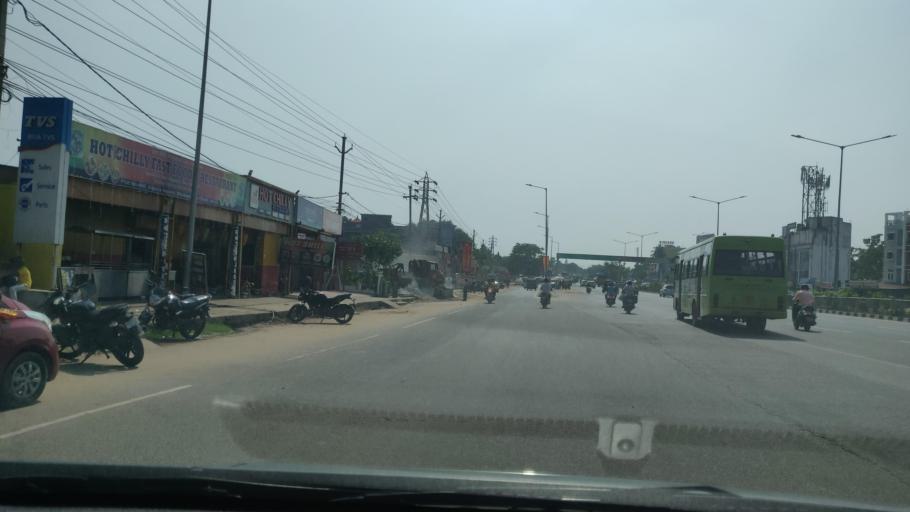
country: IN
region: Odisha
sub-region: Khordha
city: Bhubaneshwar
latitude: 20.2508
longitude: 85.7846
